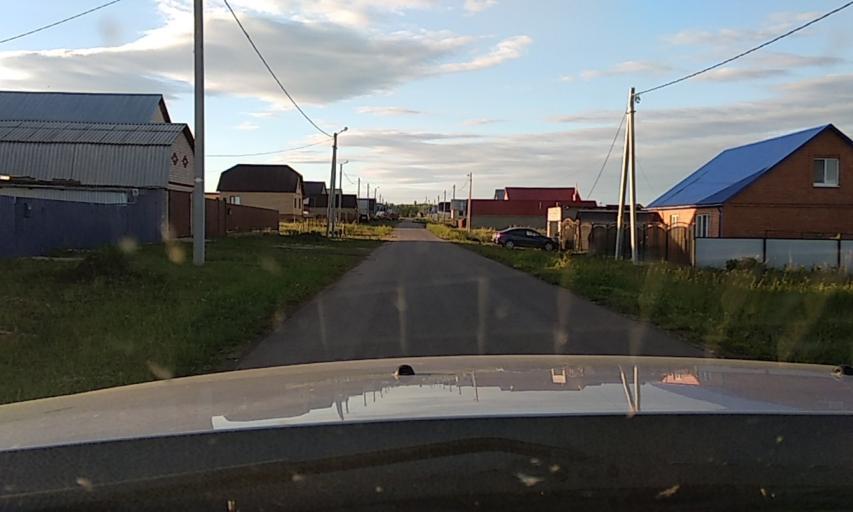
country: RU
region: Tatarstan
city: Bilyarsk
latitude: 54.8609
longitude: 50.7906
